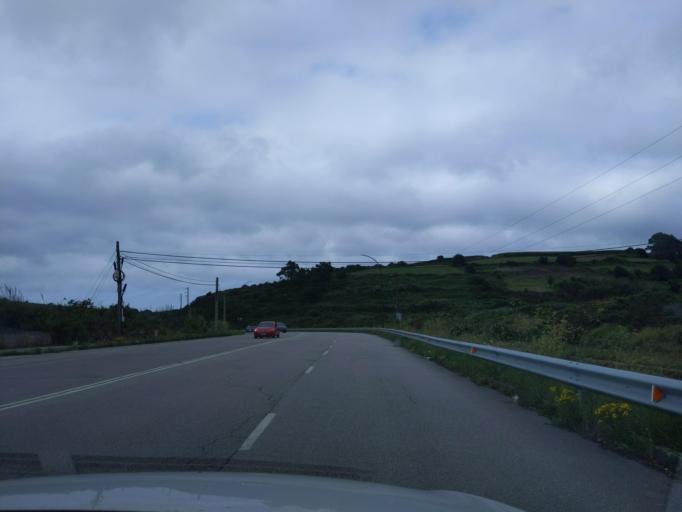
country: ES
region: Asturias
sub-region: Province of Asturias
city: Aviles
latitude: 43.5910
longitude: -5.9155
